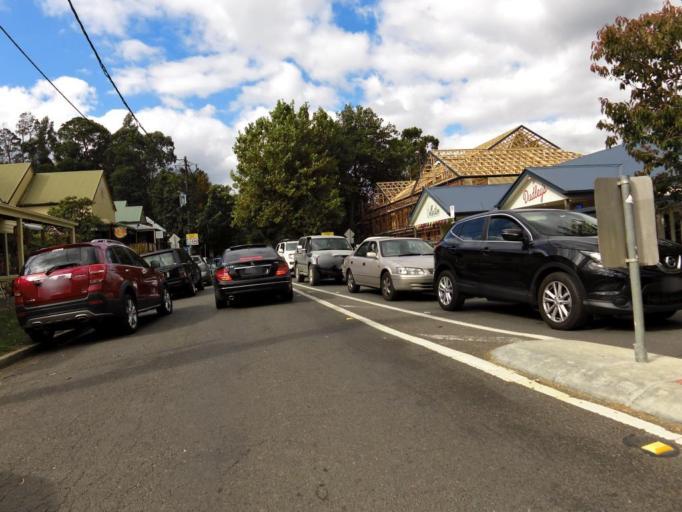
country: AU
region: Victoria
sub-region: Yarra Ranges
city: Olinda
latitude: -37.8558
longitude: 145.3652
